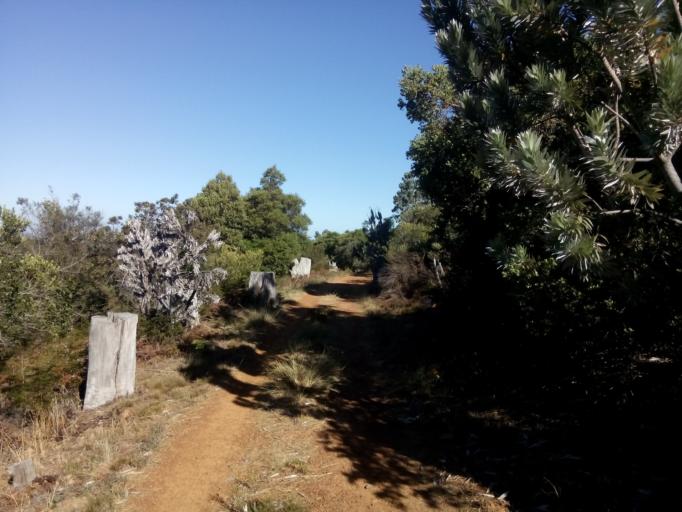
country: ZA
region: Western Cape
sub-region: City of Cape Town
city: Newlands
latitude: -33.9902
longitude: 18.4253
